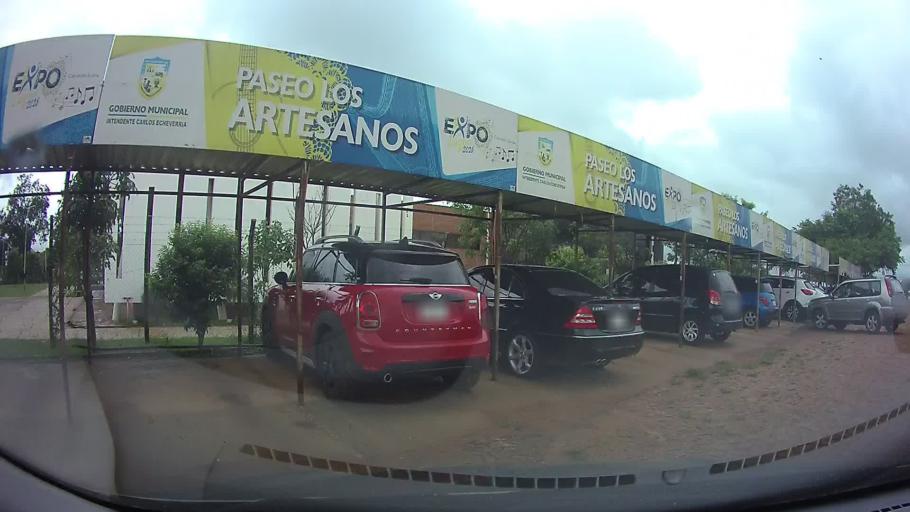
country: PY
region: Central
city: San Lorenzo
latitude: -25.2833
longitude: -57.4887
